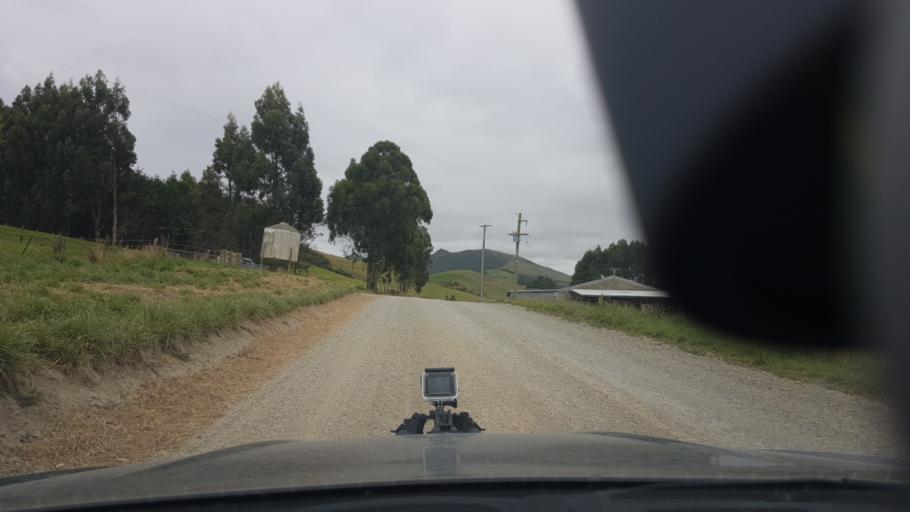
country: NZ
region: Otago
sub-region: Clutha District
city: Papatowai
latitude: -46.3437
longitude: 169.4323
